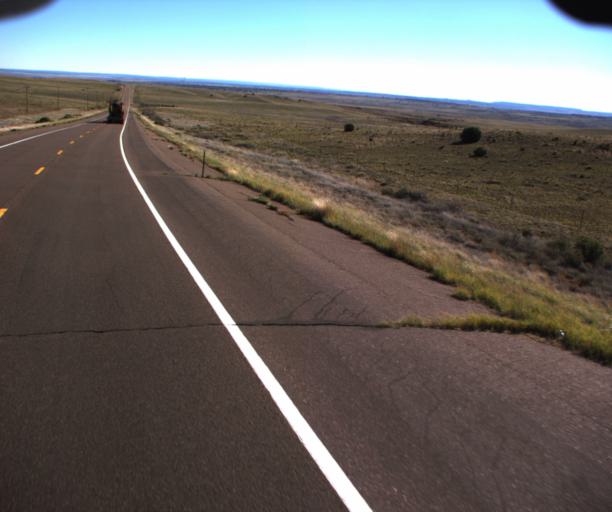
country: US
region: Arizona
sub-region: Apache County
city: Saint Johns
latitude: 34.5018
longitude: -109.4886
